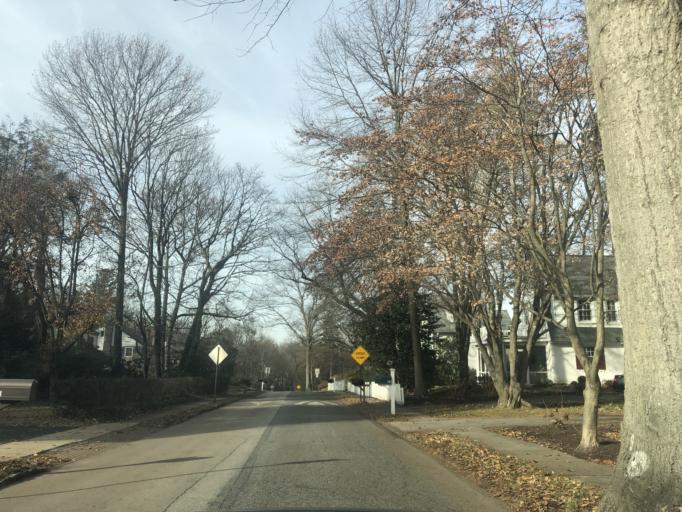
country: US
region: Pennsylvania
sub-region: Delaware County
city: Radnor
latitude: 40.0338
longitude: -75.3461
